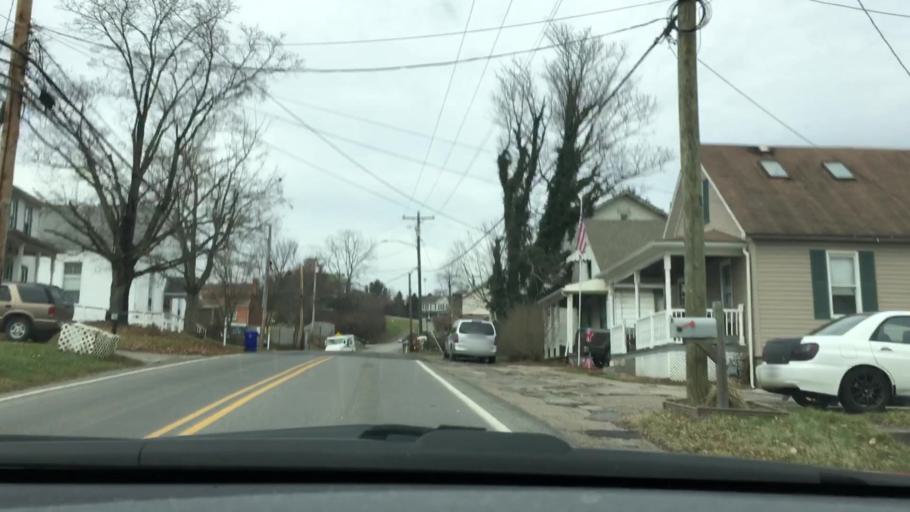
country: US
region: Pennsylvania
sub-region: Allegheny County
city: Sturgeon
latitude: 40.3906
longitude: -80.2006
